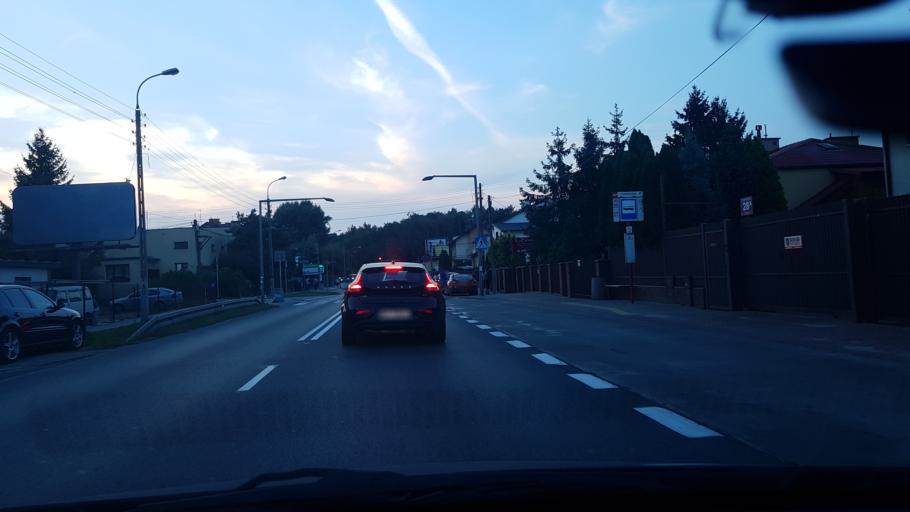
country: PL
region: Masovian Voivodeship
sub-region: Warszawa
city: Targowek
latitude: 52.2902
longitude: 21.0706
